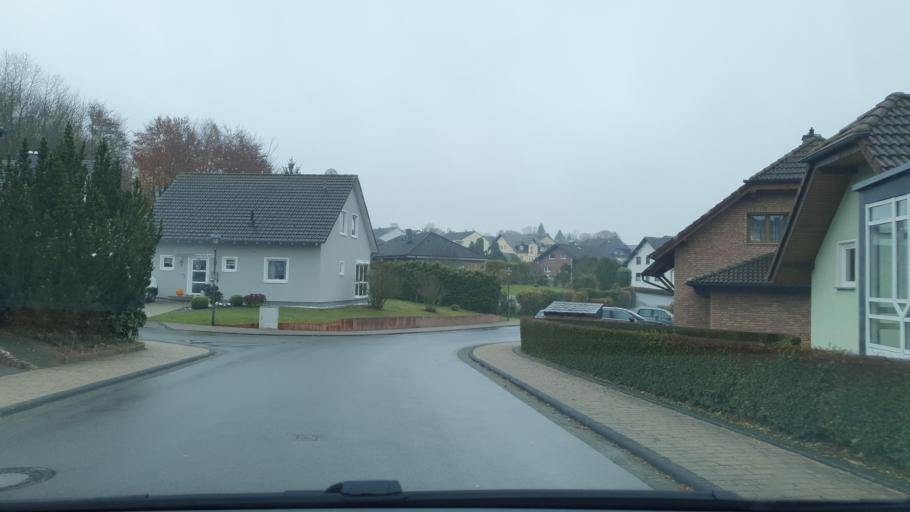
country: DE
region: Rheinland-Pfalz
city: Kirchberg
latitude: 49.9471
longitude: 7.4007
